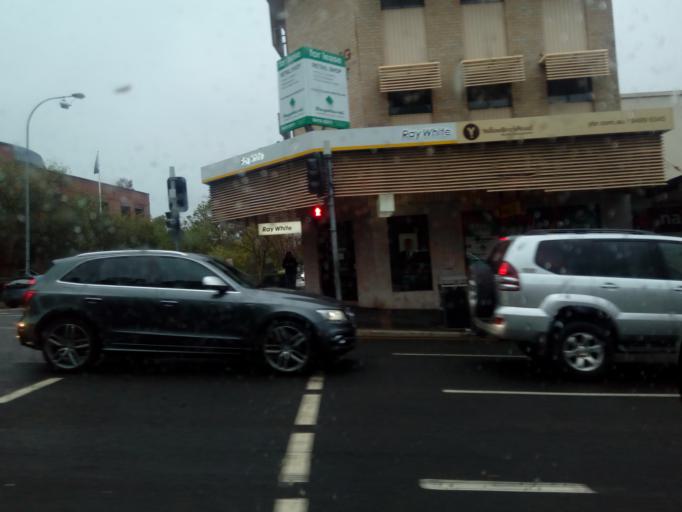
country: AU
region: New South Wales
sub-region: City of Sydney
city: Pymble
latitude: -33.7545
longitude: 151.1522
